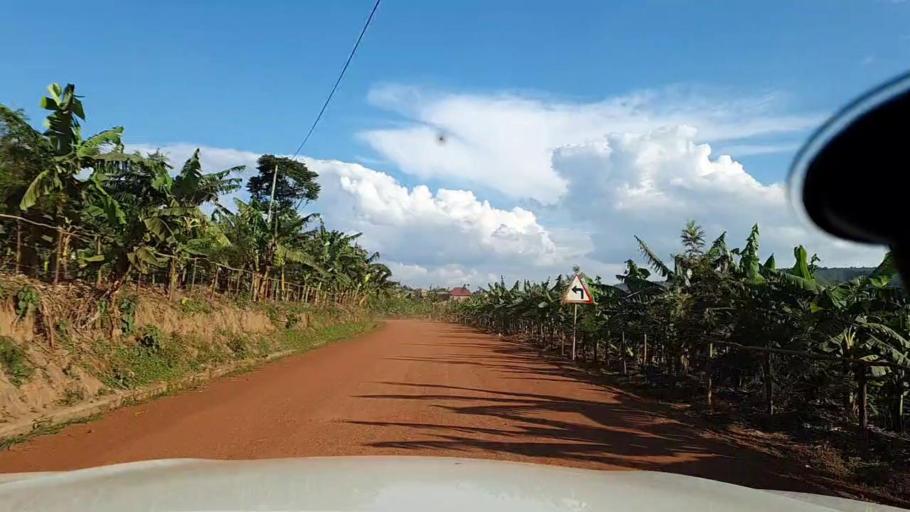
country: RW
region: Kigali
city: Kigali
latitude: -1.8608
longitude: 29.9188
